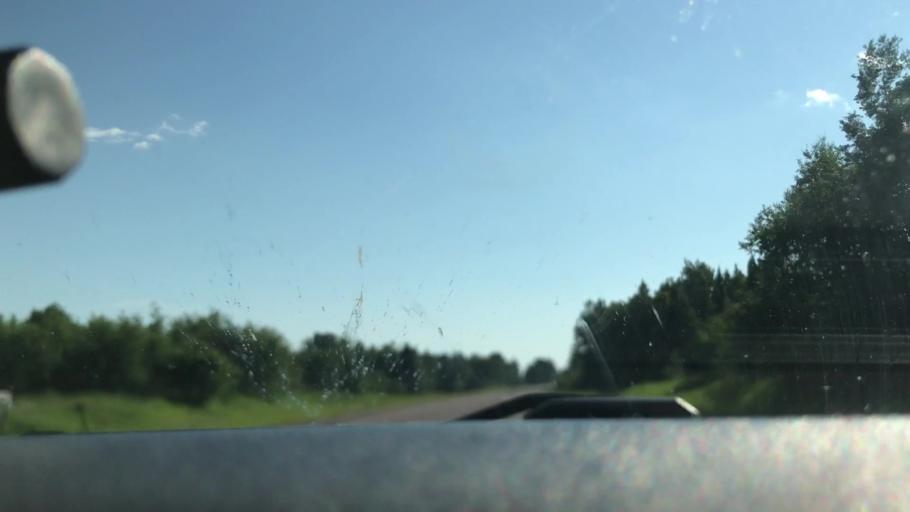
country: US
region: Minnesota
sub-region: Cook County
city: Grand Marais
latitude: 47.8022
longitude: -90.0982
